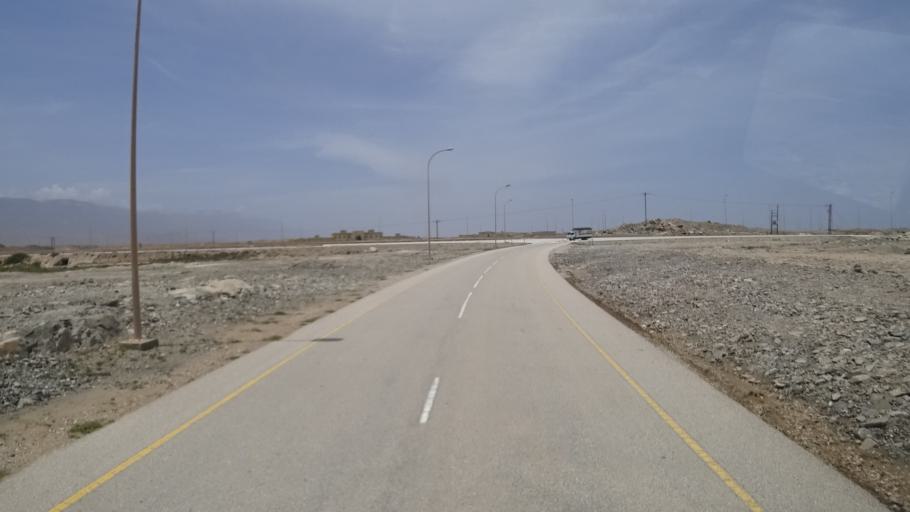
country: OM
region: Zufar
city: Salalah
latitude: 17.0085
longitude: 54.6963
